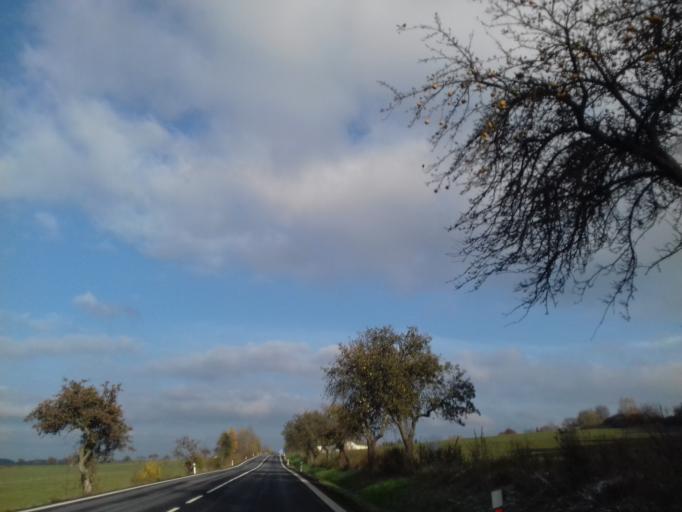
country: CZ
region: Plzensky
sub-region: Okres Domazlice
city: Klenci pod Cerchovem
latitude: 49.4526
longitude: 12.8598
